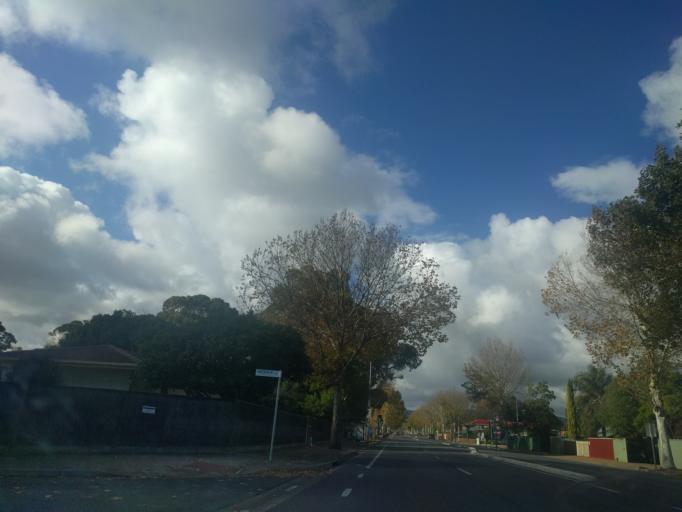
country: AU
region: South Australia
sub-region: Mitcham
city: Clarence Gardens
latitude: -34.9668
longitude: 138.5805
